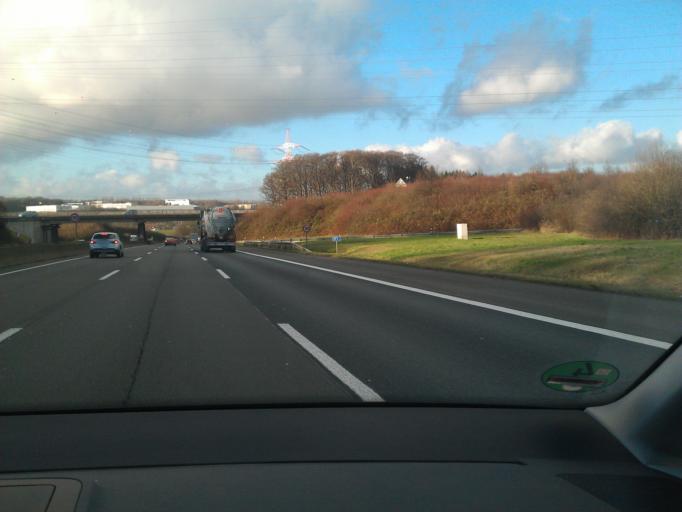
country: DE
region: North Rhine-Westphalia
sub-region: Regierungsbezirk Dusseldorf
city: Remscheid
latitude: 51.2264
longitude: 7.2366
